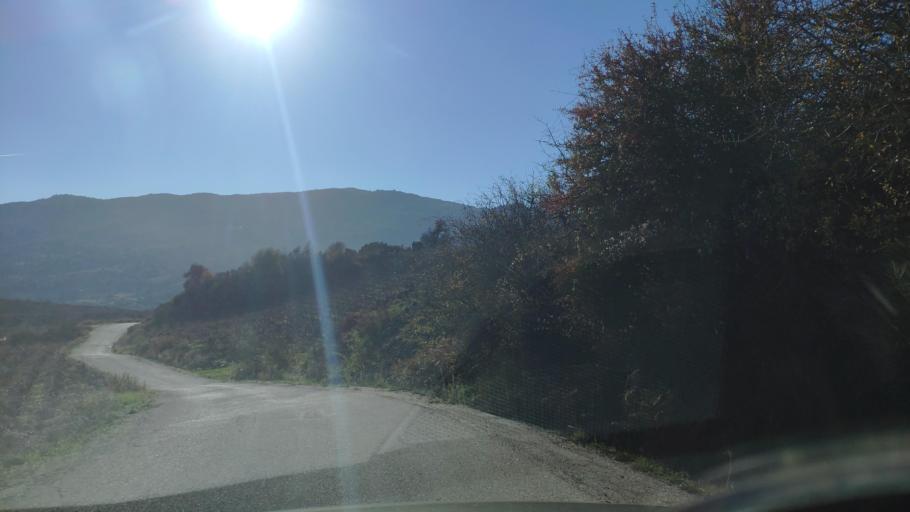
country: GR
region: Peloponnese
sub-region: Nomos Korinthias
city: Xylokastro
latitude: 38.0304
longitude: 22.4743
